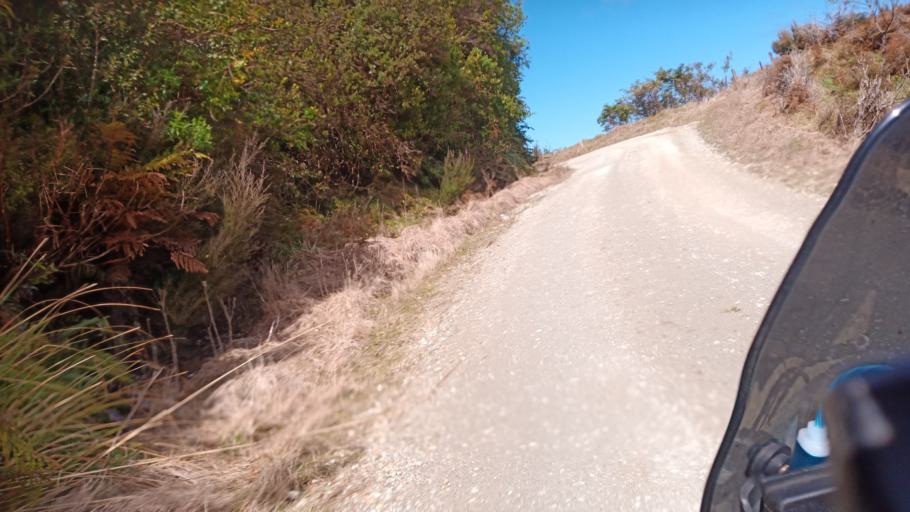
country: NZ
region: Gisborne
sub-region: Gisborne District
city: Gisborne
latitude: -38.8543
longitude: 177.7914
